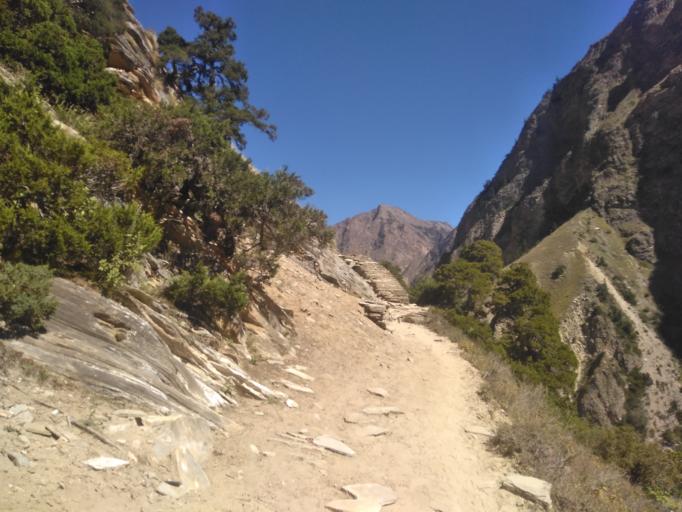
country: NP
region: Western Region
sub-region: Dhawalagiri Zone
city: Jomsom
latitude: 28.9615
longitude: 83.0732
